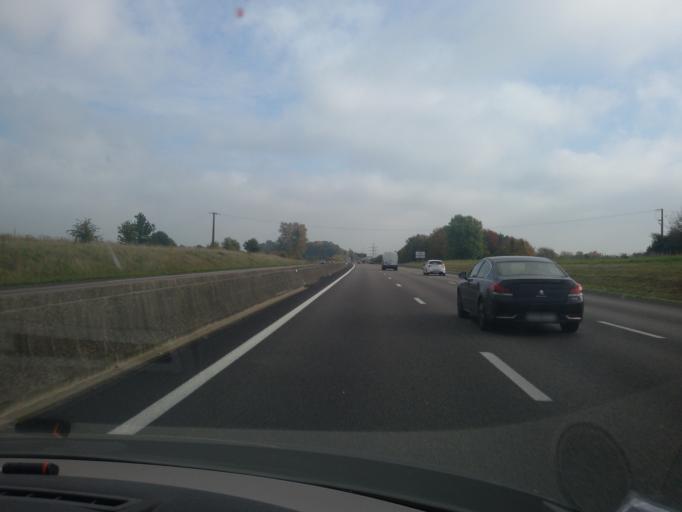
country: FR
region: Haute-Normandie
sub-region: Departement de l'Eure
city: Saint-Ouen-de-Thouberville
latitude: 49.3507
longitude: 0.8942
